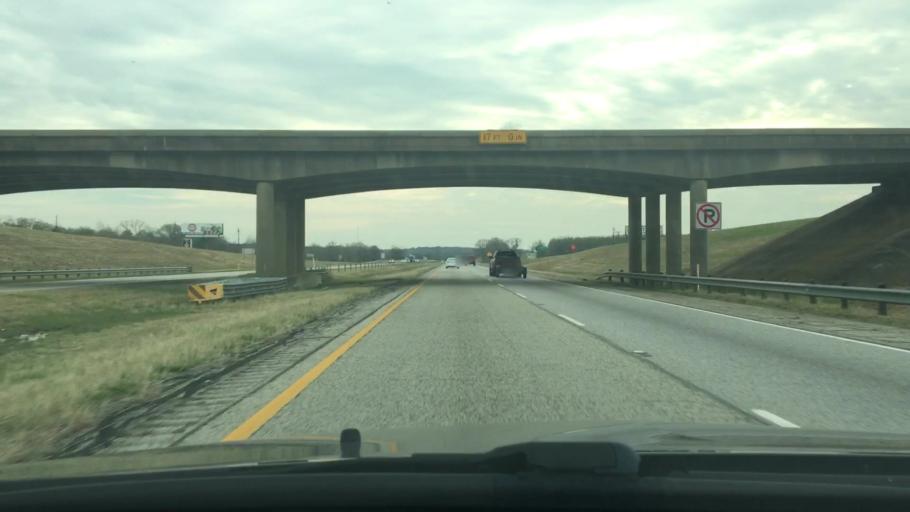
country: US
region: Texas
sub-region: Leon County
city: Centerville
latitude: 31.2584
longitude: -95.9881
